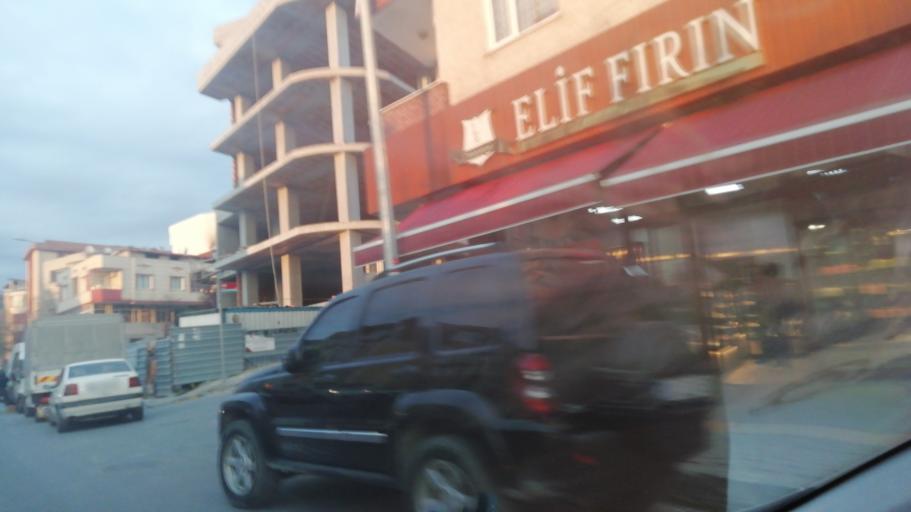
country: TR
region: Istanbul
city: Mahmutbey
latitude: 41.0366
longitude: 28.8233
